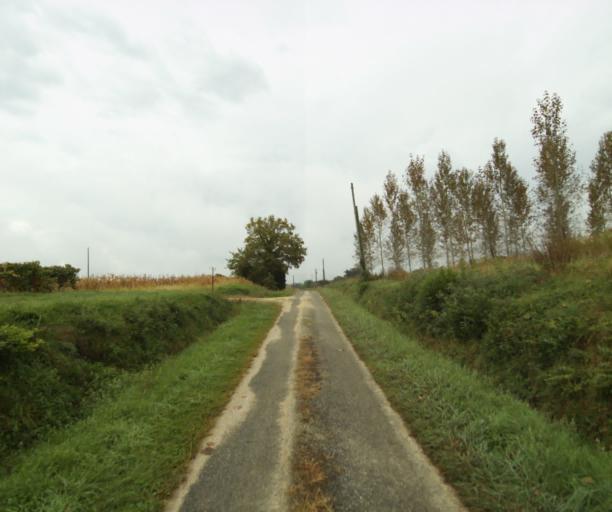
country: FR
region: Midi-Pyrenees
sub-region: Departement du Gers
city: Cazaubon
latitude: 43.9309
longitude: -0.1427
